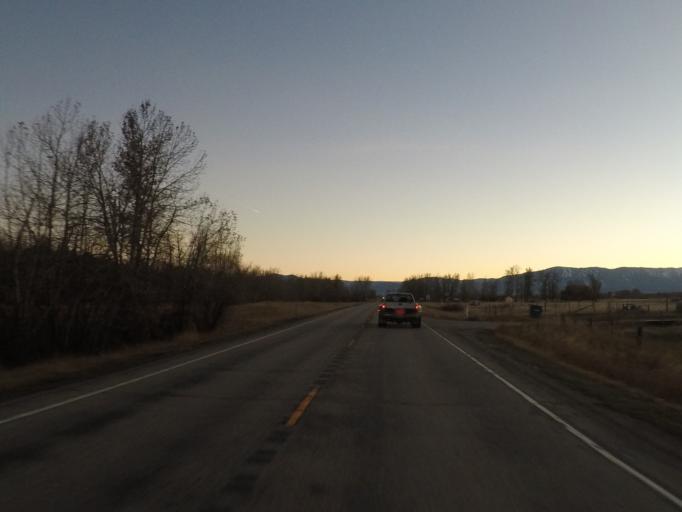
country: US
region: Montana
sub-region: Carbon County
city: Red Lodge
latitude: 45.3231
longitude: -109.1900
